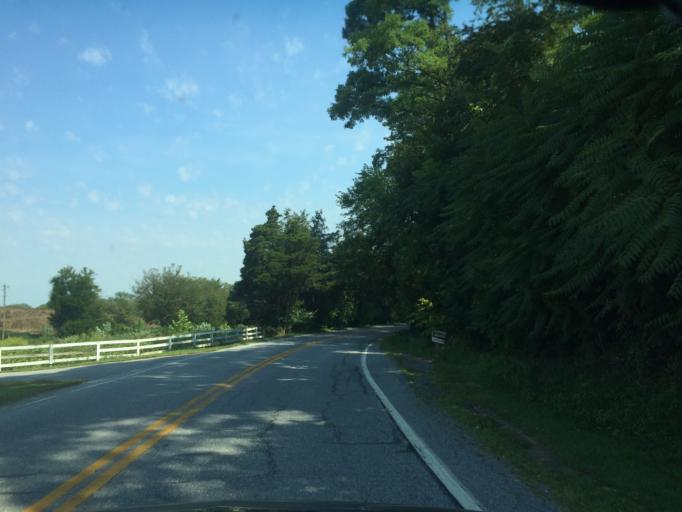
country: US
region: Maryland
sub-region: Carroll County
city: New Windsor
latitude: 39.6057
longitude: -77.1163
